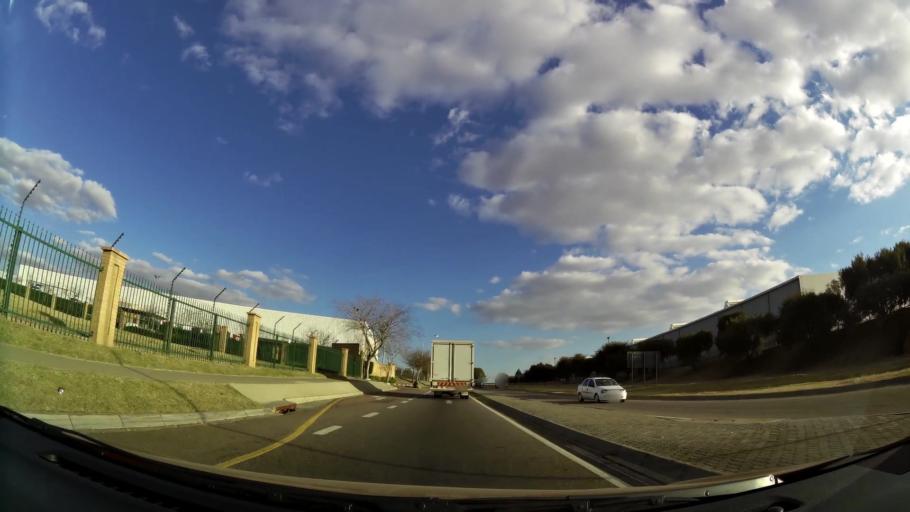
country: ZA
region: Gauteng
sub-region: City of Tshwane Metropolitan Municipality
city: Centurion
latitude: -25.9119
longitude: 28.1647
